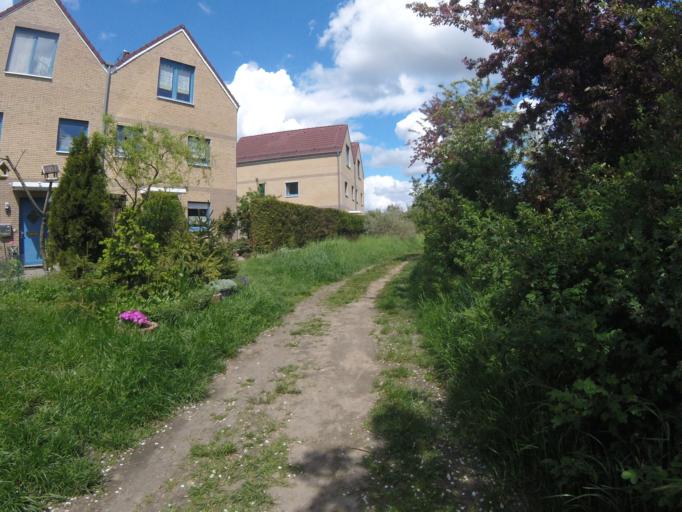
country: DE
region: Brandenburg
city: Konigs Wusterhausen
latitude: 52.2980
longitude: 13.6007
